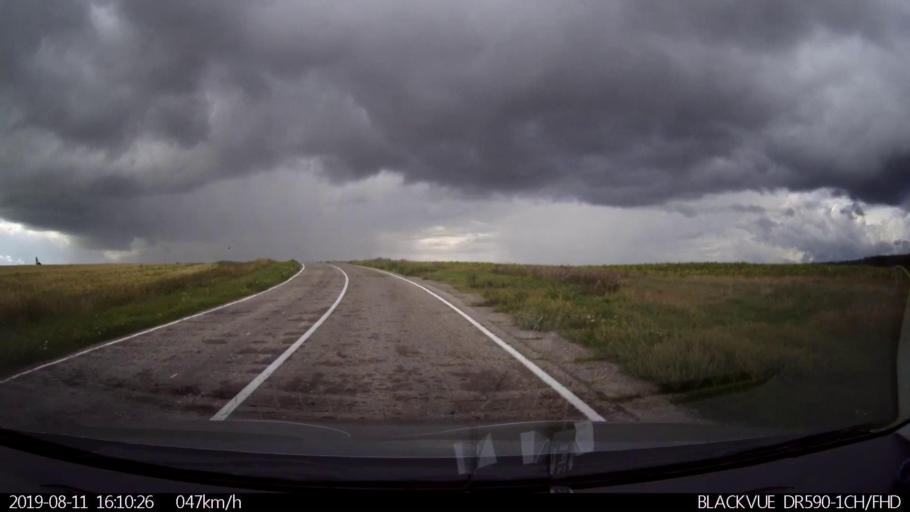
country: RU
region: Ulyanovsk
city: Ignatovka
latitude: 53.9986
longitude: 47.6550
